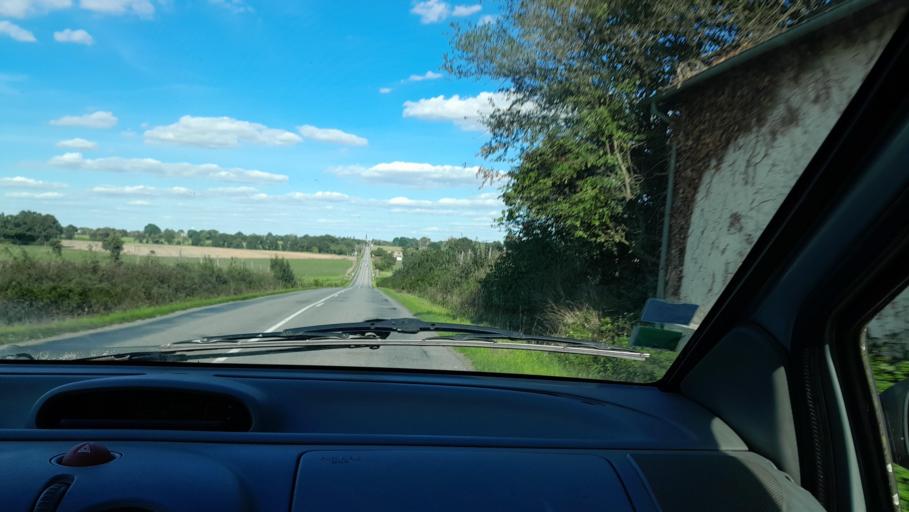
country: FR
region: Pays de la Loire
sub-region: Departement de la Mayenne
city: Ballots
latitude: 47.9553
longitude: -1.0629
